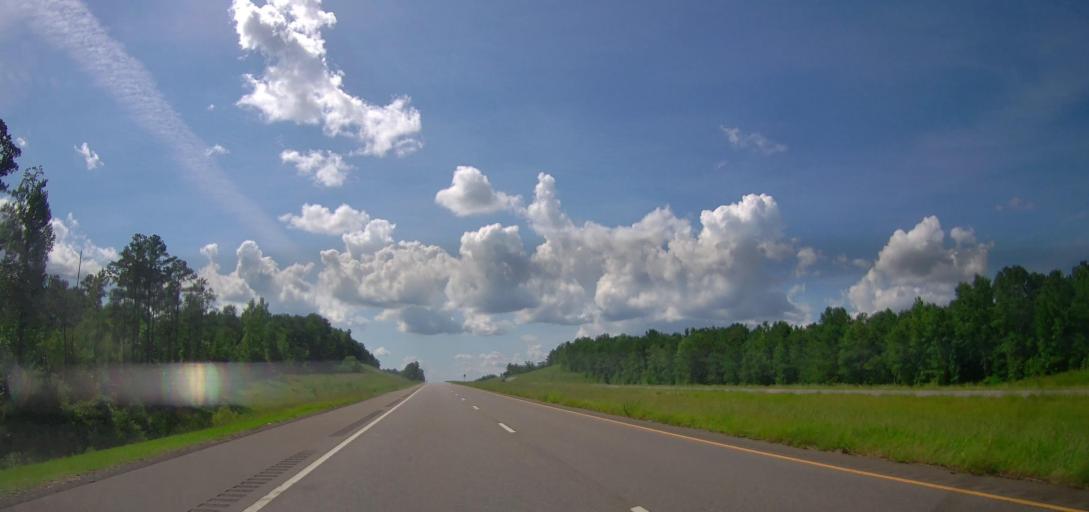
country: US
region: Alabama
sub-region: Pickens County
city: Reform
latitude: 33.3556
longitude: -87.9663
